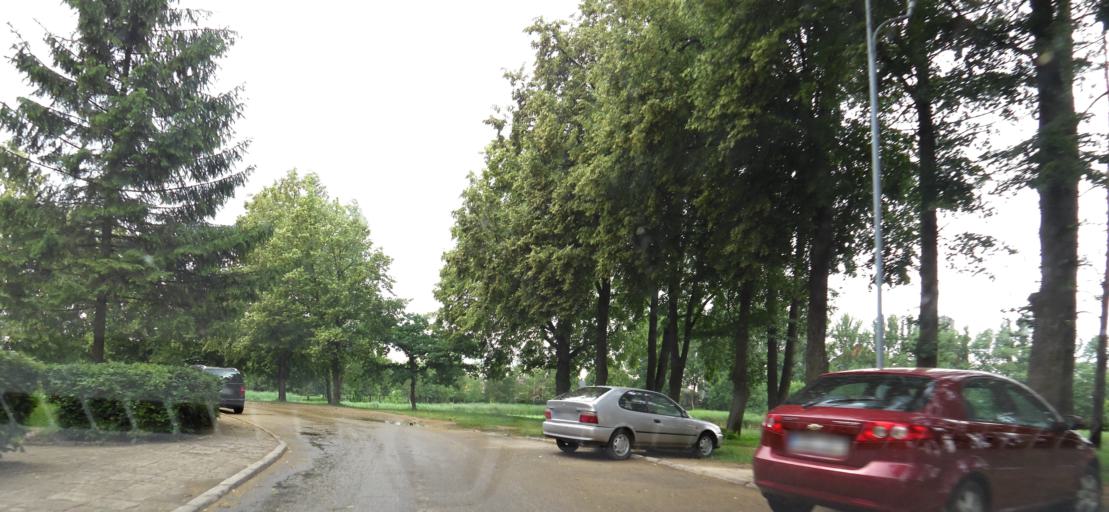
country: LT
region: Panevezys
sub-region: Birzai
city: Birzai
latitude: 56.1965
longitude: 24.7516
